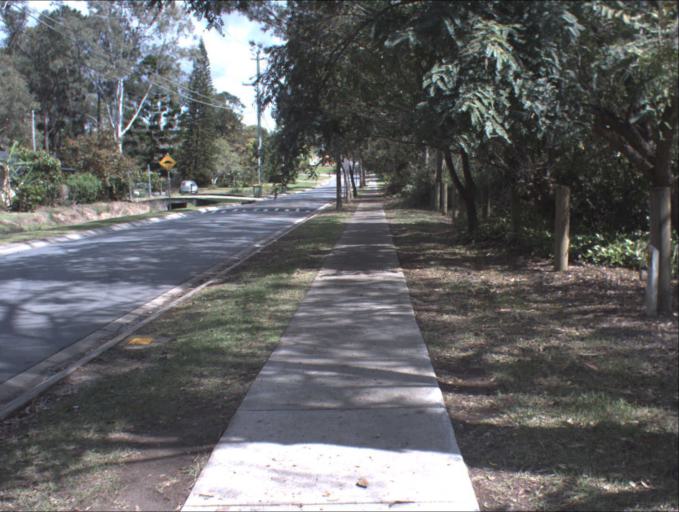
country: AU
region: Queensland
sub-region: Logan
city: Park Ridge South
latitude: -27.6709
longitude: 153.0270
